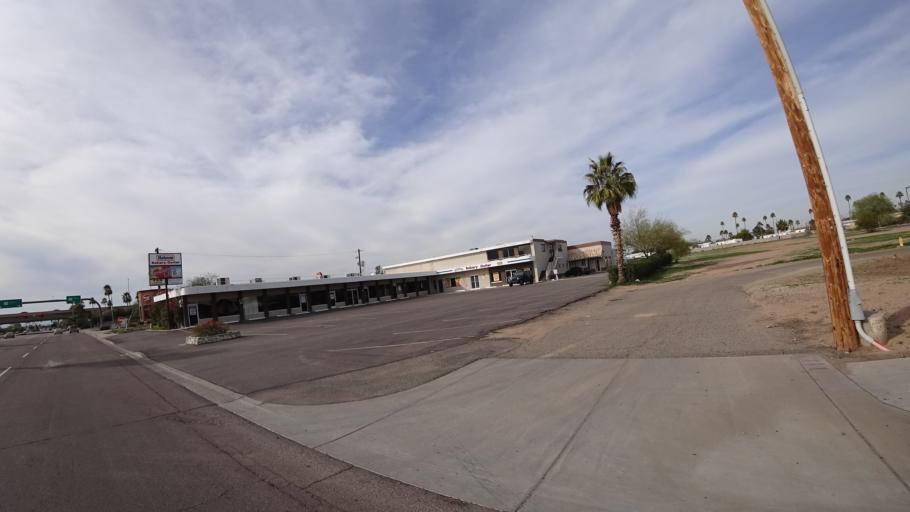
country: US
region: Arizona
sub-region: Maricopa County
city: Peoria
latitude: 33.5808
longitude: -112.2569
